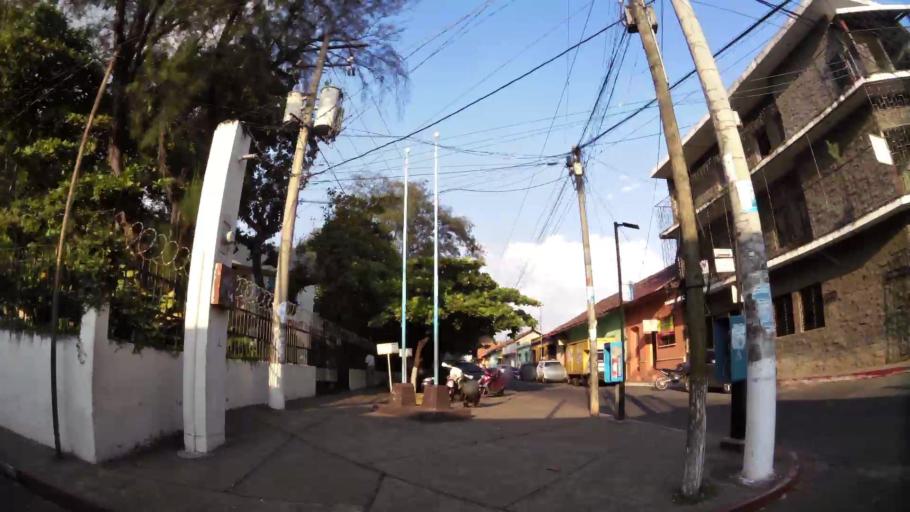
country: GT
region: Retalhuleu
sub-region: Municipio de Retalhuleu
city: Retalhuleu
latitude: 14.5349
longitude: -91.6776
